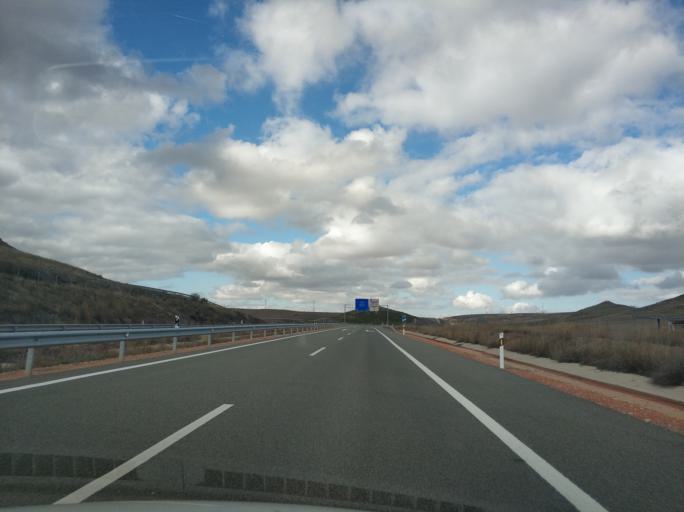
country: ES
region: Castille and Leon
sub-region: Provincia de Soria
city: Yelo
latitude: 41.2130
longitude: -2.4676
